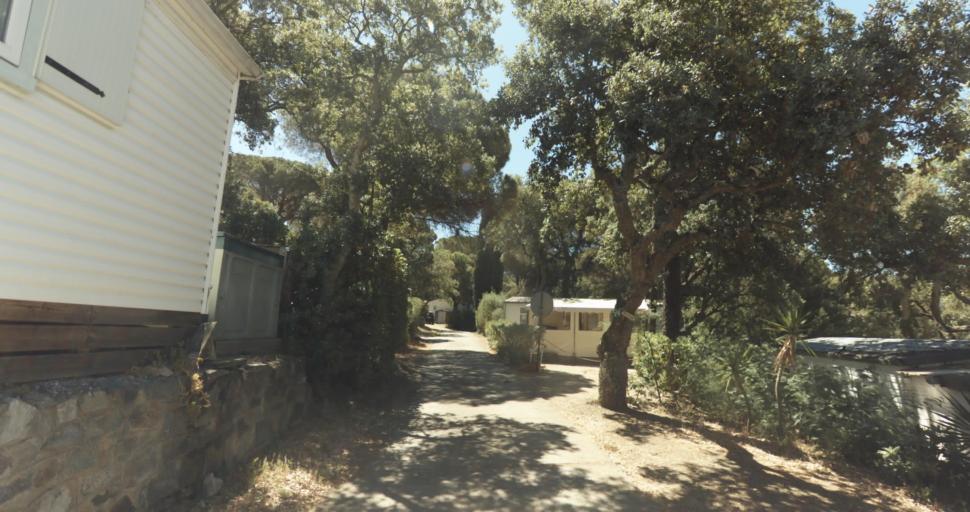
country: FR
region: Provence-Alpes-Cote d'Azur
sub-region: Departement du Var
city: Gassin
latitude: 43.2427
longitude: 6.5746
